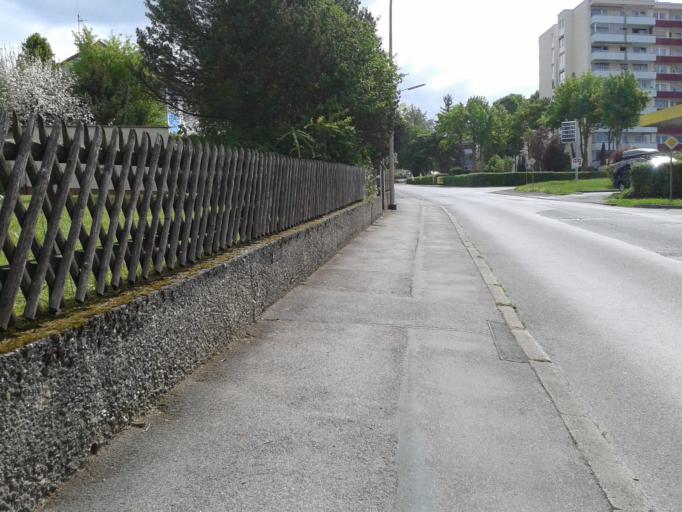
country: DE
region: Bavaria
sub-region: Upper Franconia
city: Kronach
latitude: 50.2400
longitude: 11.3402
